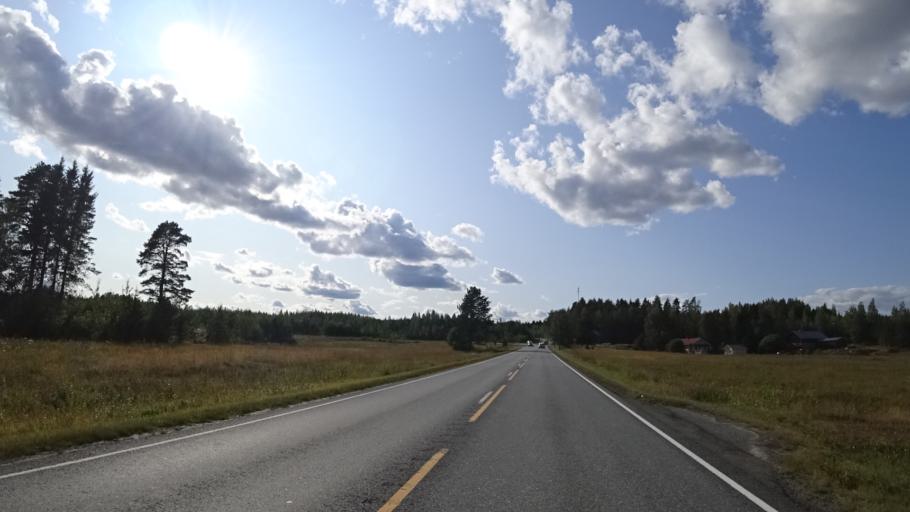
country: FI
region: North Karelia
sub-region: Keski-Karjala
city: Kitee
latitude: 62.0911
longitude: 29.9638
